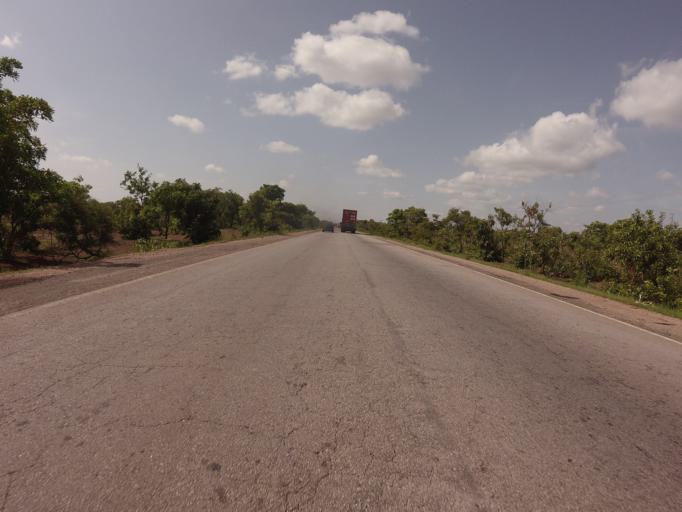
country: GH
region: Northern
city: Savelugu
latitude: 9.9508
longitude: -0.8366
